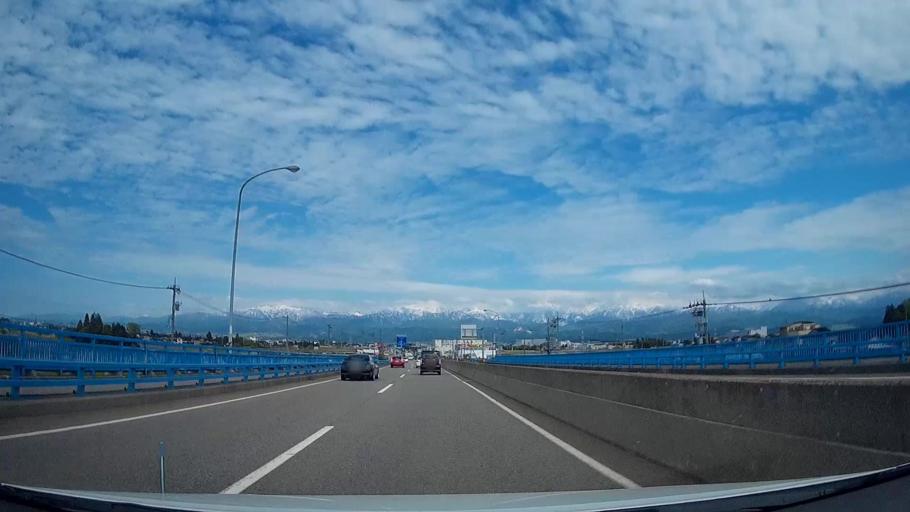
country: JP
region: Toyama
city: Toyama-shi
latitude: 36.7182
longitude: 137.2780
